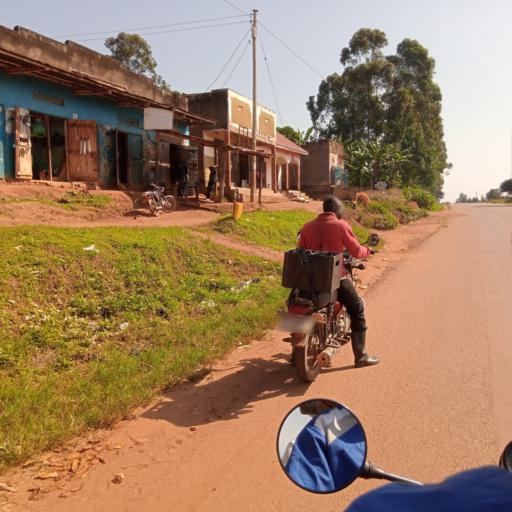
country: UG
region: Central Region
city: Masaka
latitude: -0.3710
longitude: 31.7159
